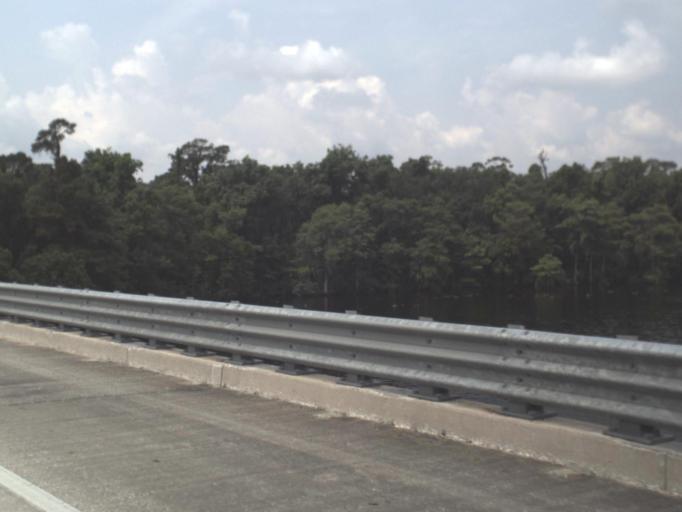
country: US
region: Florida
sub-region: Clay County
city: Green Cove Springs
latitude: 30.0406
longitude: -81.7090
